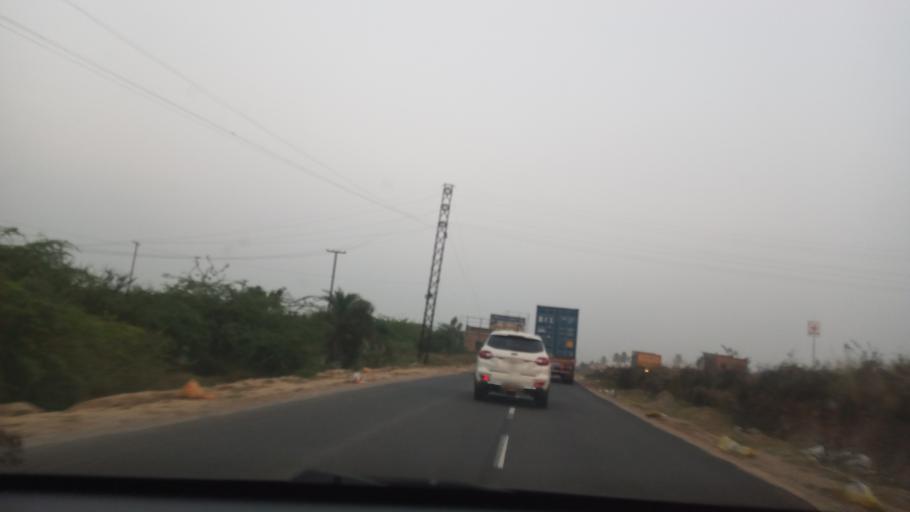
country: IN
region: Tamil Nadu
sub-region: Kancheepuram
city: Kanchipuram
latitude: 12.8745
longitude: 79.6278
